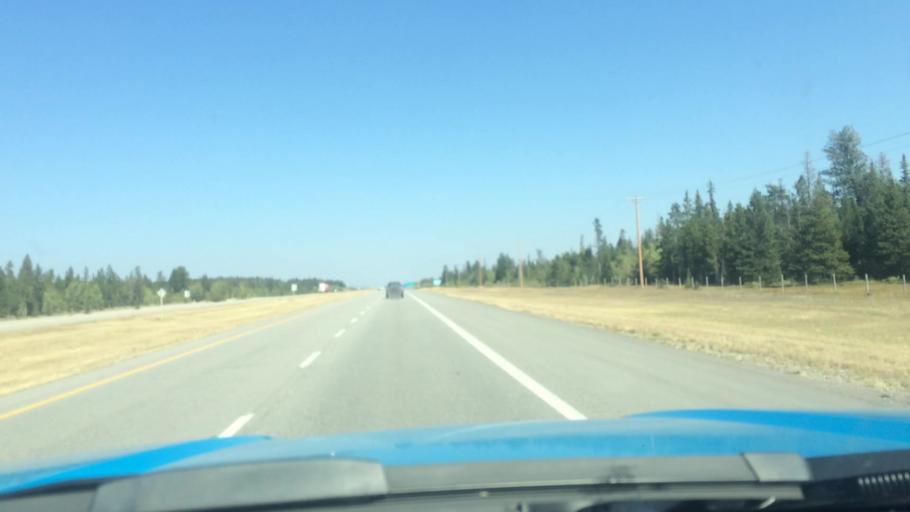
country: CA
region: Alberta
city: Canmore
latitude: 51.0935
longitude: -115.0460
